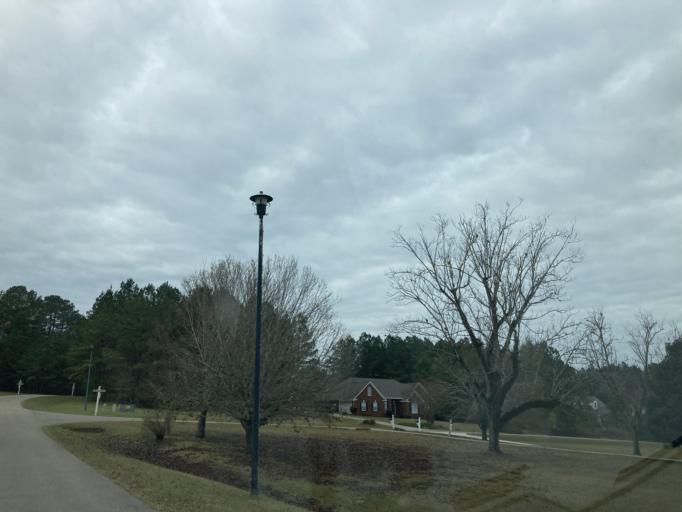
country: US
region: Mississippi
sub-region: Forrest County
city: Hattiesburg
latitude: 31.2504
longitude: -89.2986
